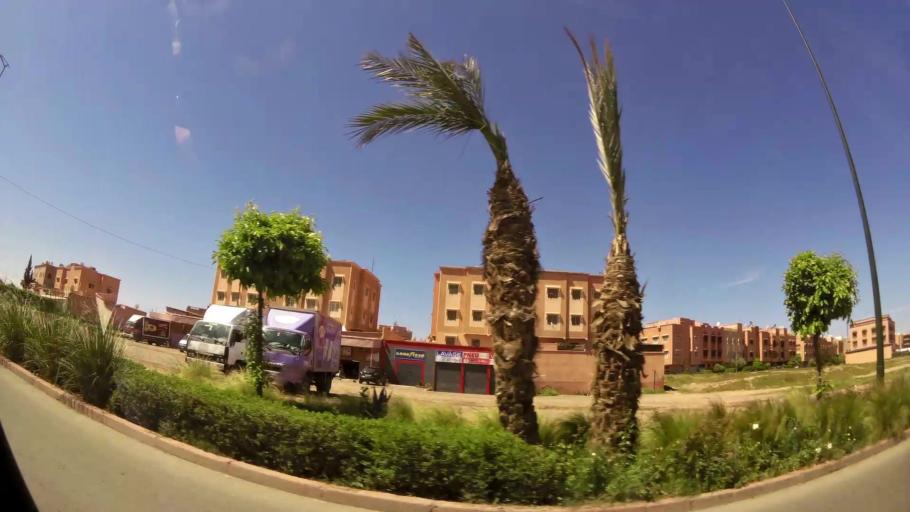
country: MA
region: Marrakech-Tensift-Al Haouz
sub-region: Marrakech
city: Marrakesh
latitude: 31.6605
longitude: -7.9848
